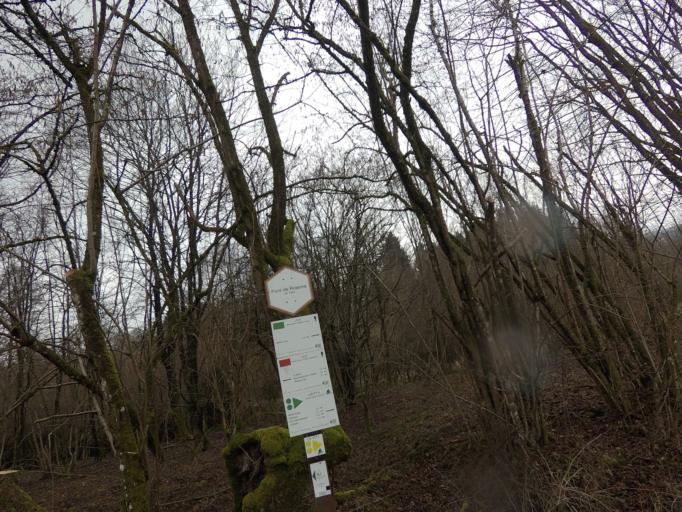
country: BE
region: Wallonia
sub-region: Province de Liege
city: Trois-Ponts
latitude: 50.4159
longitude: 5.8653
